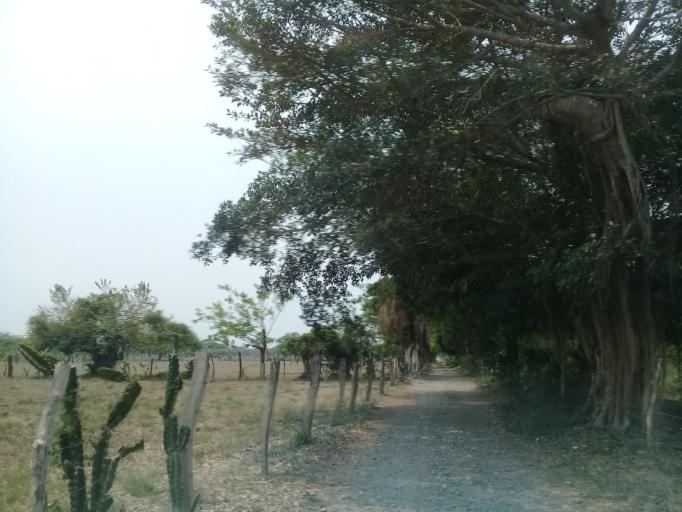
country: MX
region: Veracruz
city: Jamapa
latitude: 18.9251
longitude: -96.2017
